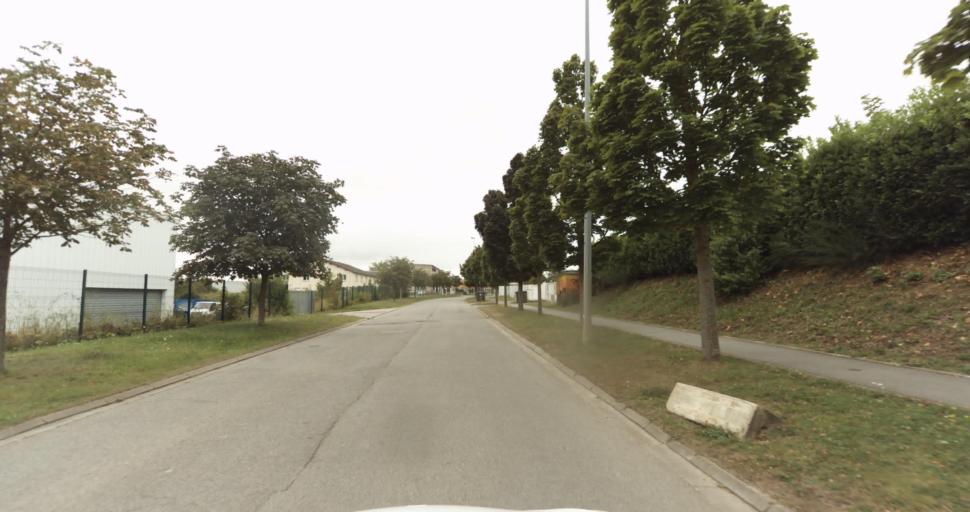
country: FR
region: Haute-Normandie
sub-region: Departement de l'Eure
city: Gravigny
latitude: 49.0328
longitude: 1.1832
